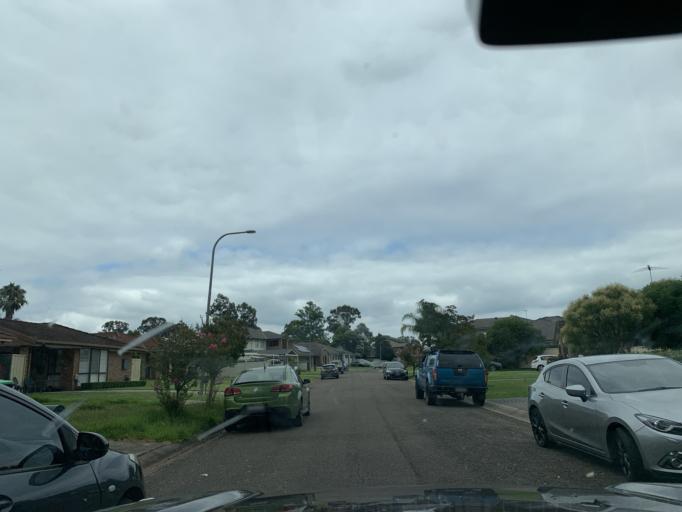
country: AU
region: New South Wales
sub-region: Penrith Municipality
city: Werrington Downs
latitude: -33.7061
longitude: 150.7153
